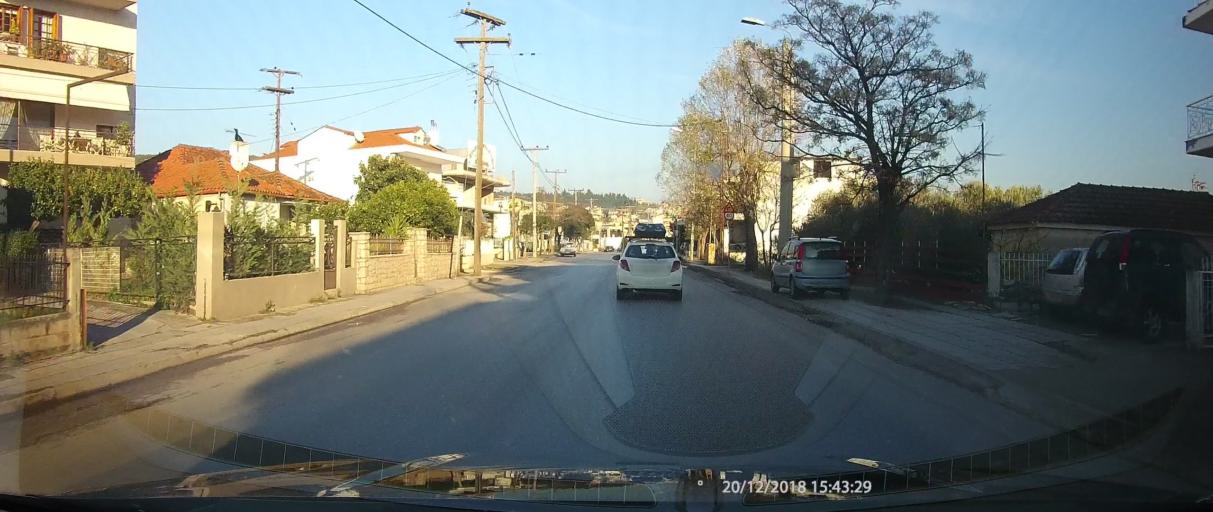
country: GR
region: Central Greece
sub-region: Nomos Fthiotidos
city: Lamia
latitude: 38.8916
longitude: 22.4088
